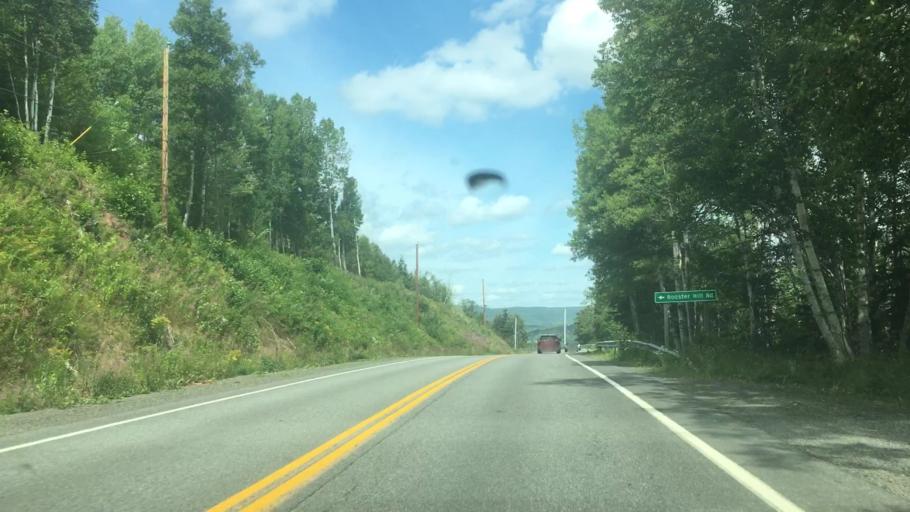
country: CA
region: Nova Scotia
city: Sydney Mines
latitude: 46.2707
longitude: -60.6095
